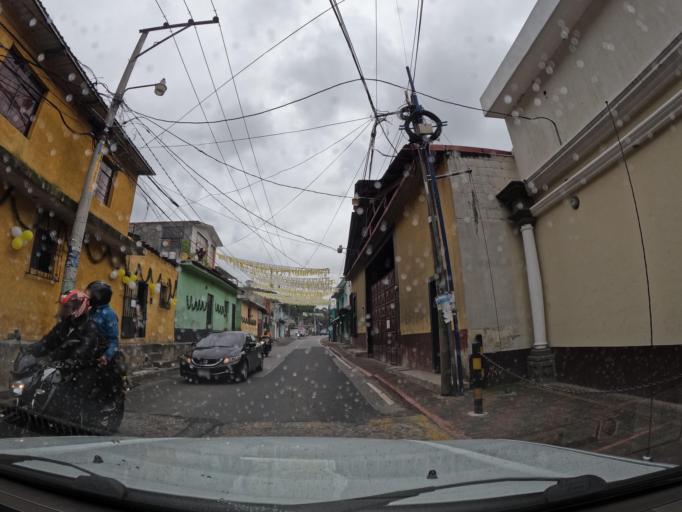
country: GT
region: Sacatepequez
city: Pastores
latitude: 14.6038
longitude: -90.7633
